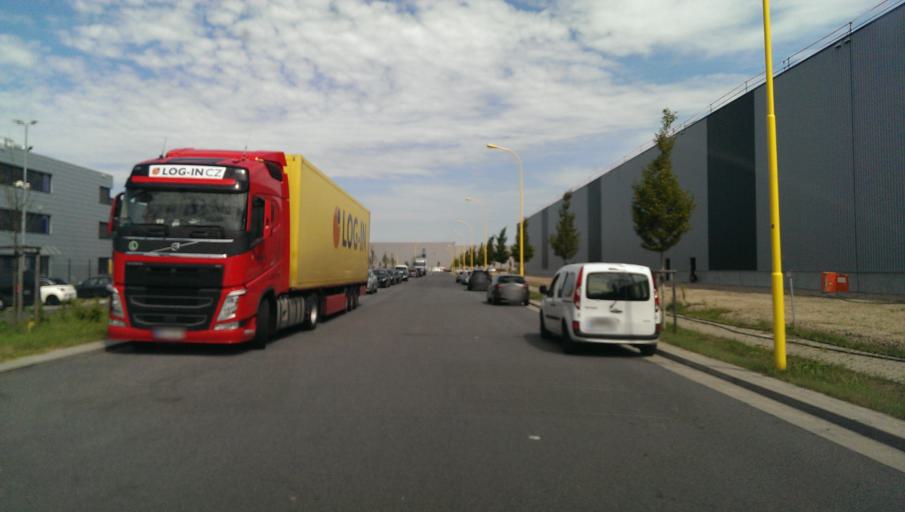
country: DE
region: Brandenburg
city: Grossbeeren
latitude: 52.3742
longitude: 13.3244
